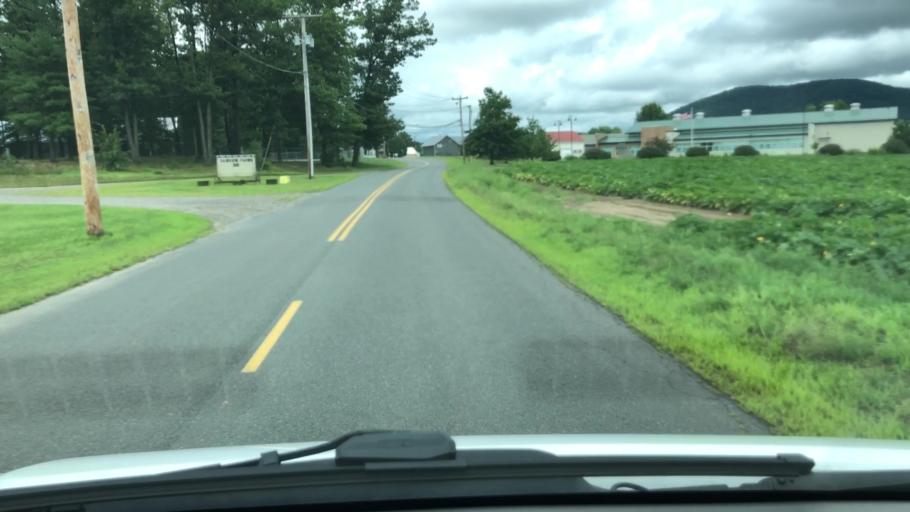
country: US
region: Massachusetts
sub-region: Franklin County
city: South Deerfield
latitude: 42.4600
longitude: -72.6088
